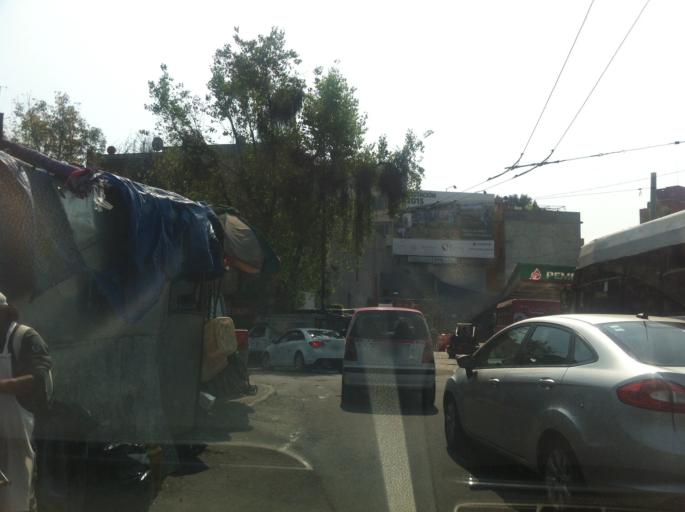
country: MX
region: Mexico City
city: Polanco
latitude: 19.4207
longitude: -99.1764
